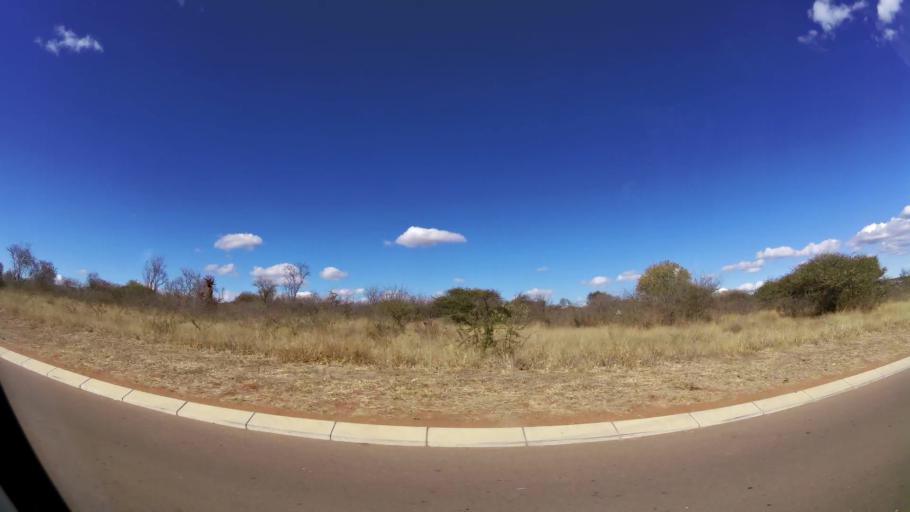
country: ZA
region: Limpopo
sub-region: Capricorn District Municipality
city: Polokwane
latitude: -23.8703
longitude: 29.4958
